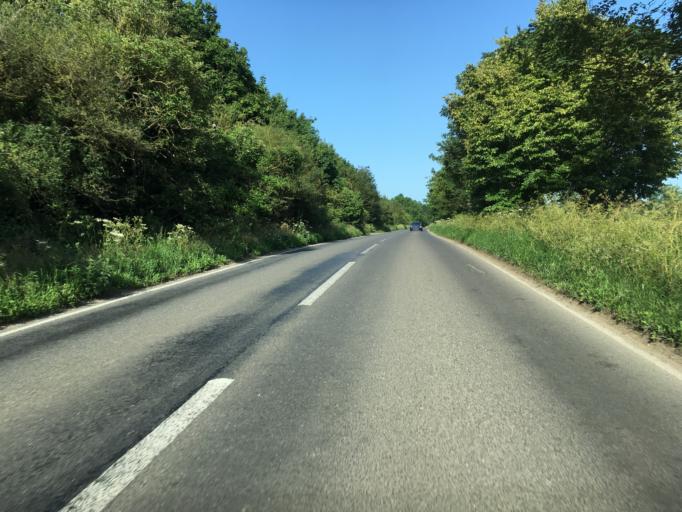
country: GB
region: England
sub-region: Oxfordshire
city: Stonesfield
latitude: 51.9234
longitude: -1.4308
